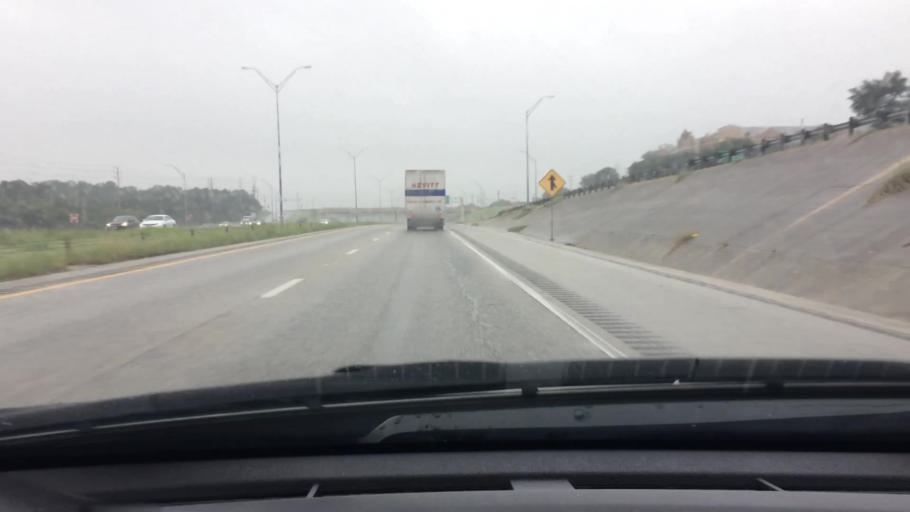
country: US
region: Texas
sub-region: Bexar County
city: Leon Valley
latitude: 29.4714
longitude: -98.6961
